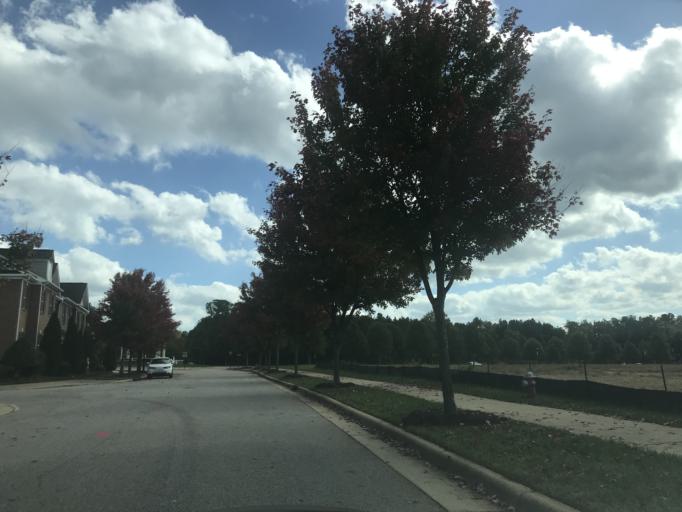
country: US
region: North Carolina
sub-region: Wake County
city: Raleigh
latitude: 35.7347
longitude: -78.6575
